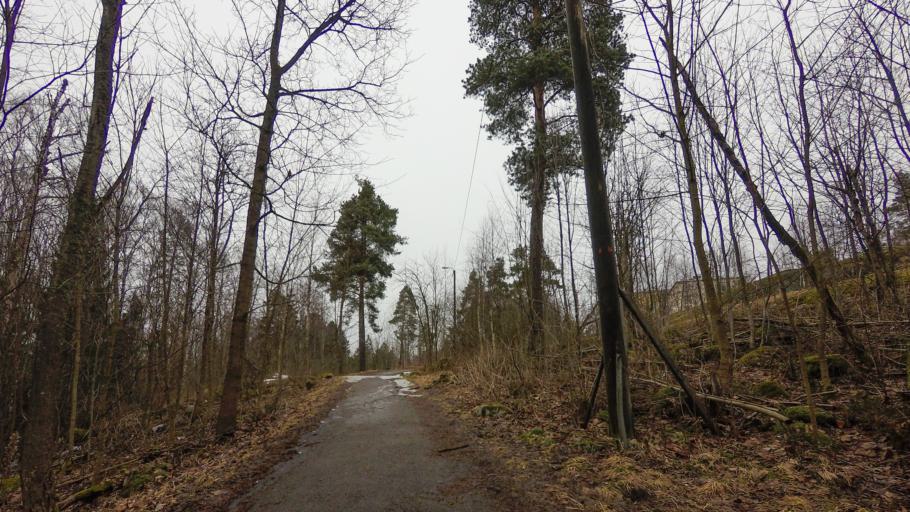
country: FI
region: Uusimaa
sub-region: Helsinki
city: Vantaa
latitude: 60.2009
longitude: 25.0271
